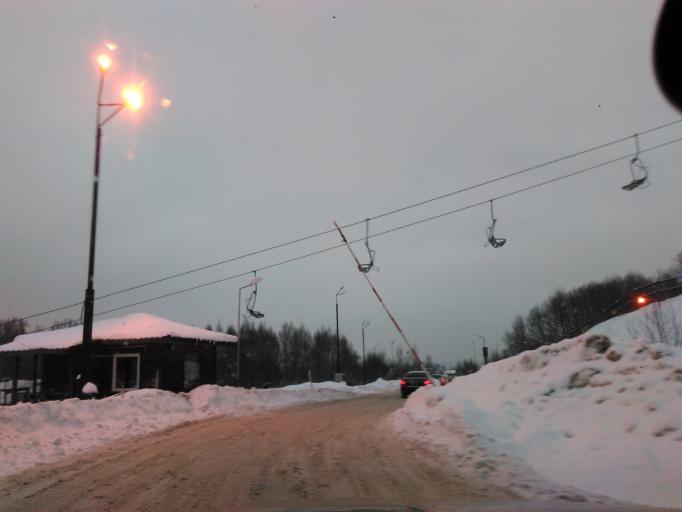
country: RU
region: Moskovskaya
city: Yakhroma
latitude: 56.2606
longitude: 37.4312
